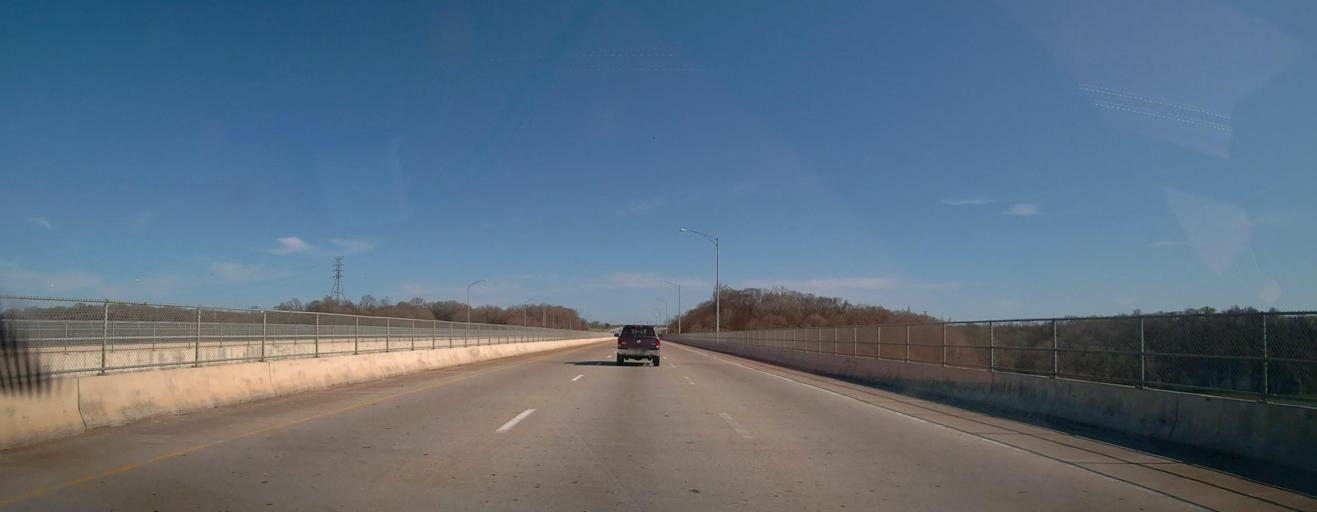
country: US
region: Alabama
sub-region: Lauderdale County
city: East Florence
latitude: 34.7940
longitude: -87.6448
